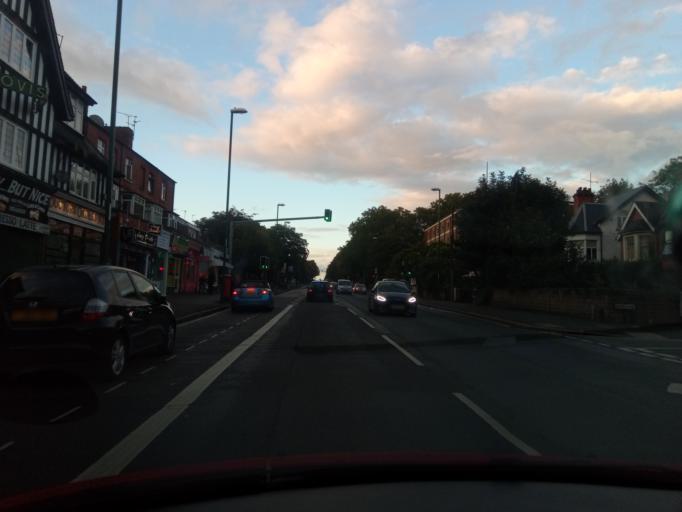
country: GB
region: England
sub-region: Nottingham
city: Nottingham
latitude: 52.9726
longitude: -1.1523
